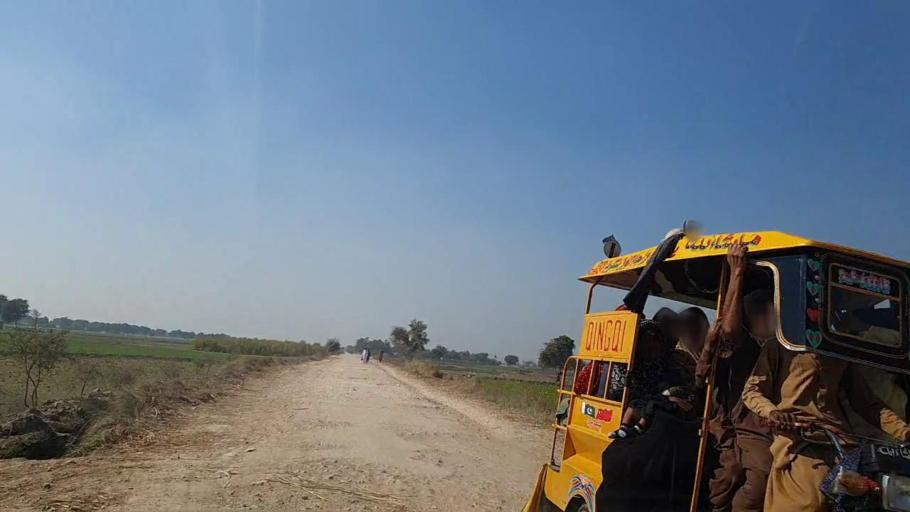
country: PK
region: Sindh
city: Sakrand
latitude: 26.2906
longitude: 68.0888
